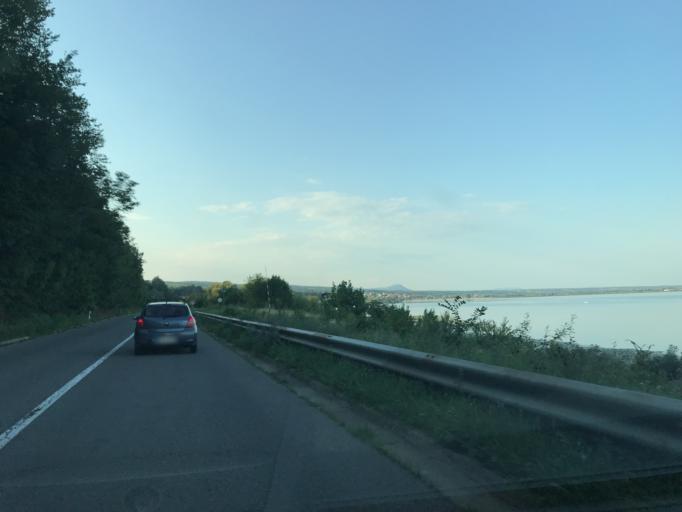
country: RO
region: Mehedinti
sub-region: Comuna Gogosu
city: Ostrovu Mare
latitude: 44.4656
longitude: 22.4503
